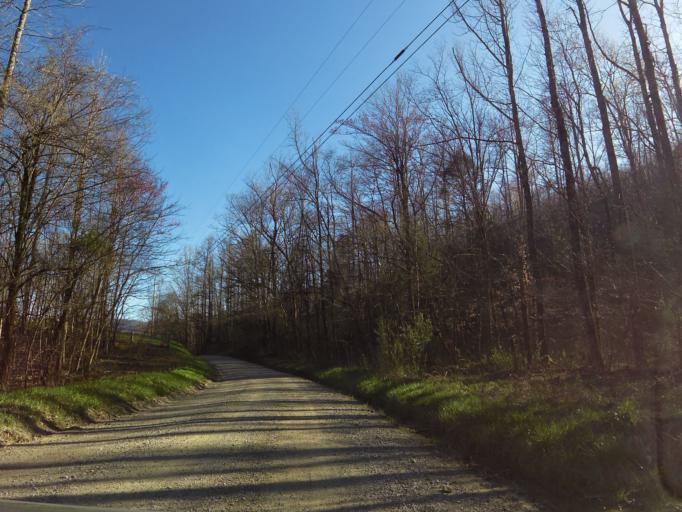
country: US
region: Tennessee
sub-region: Campbell County
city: Caryville
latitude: 36.2562
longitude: -84.3955
